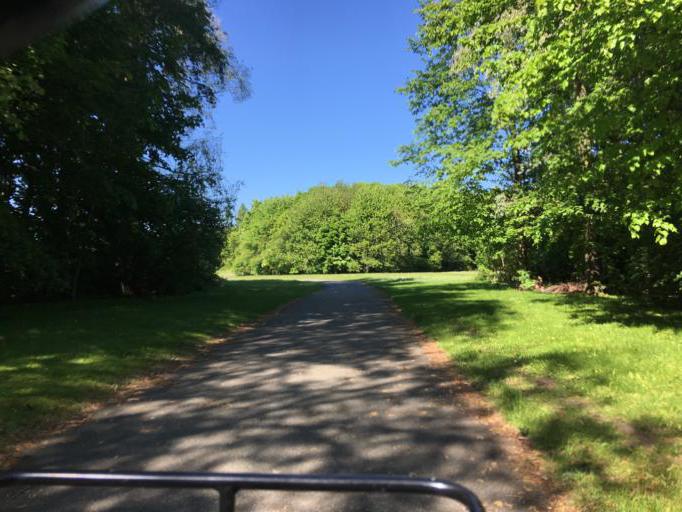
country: SE
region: Skane
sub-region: Malmo
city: Malmoe
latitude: 55.5734
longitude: 13.0525
